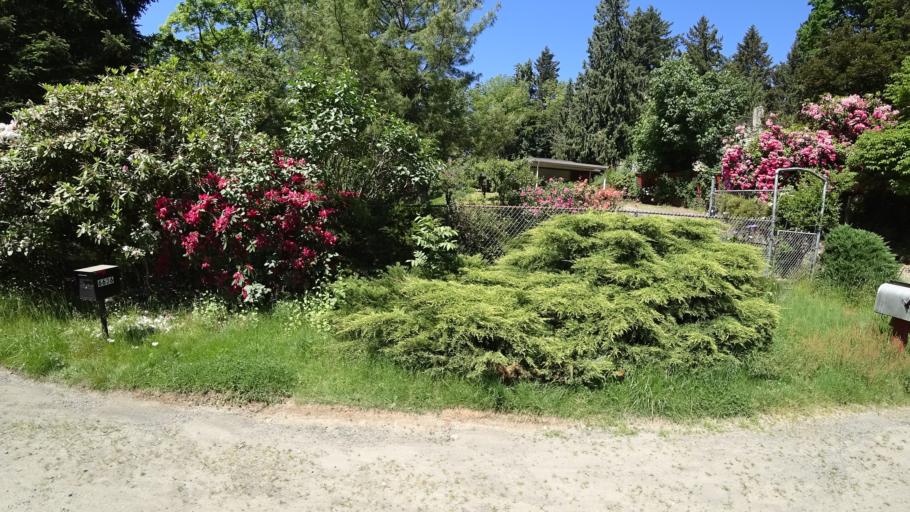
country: US
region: Oregon
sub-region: Clackamas County
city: Happy Valley
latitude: 45.4745
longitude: -122.5172
